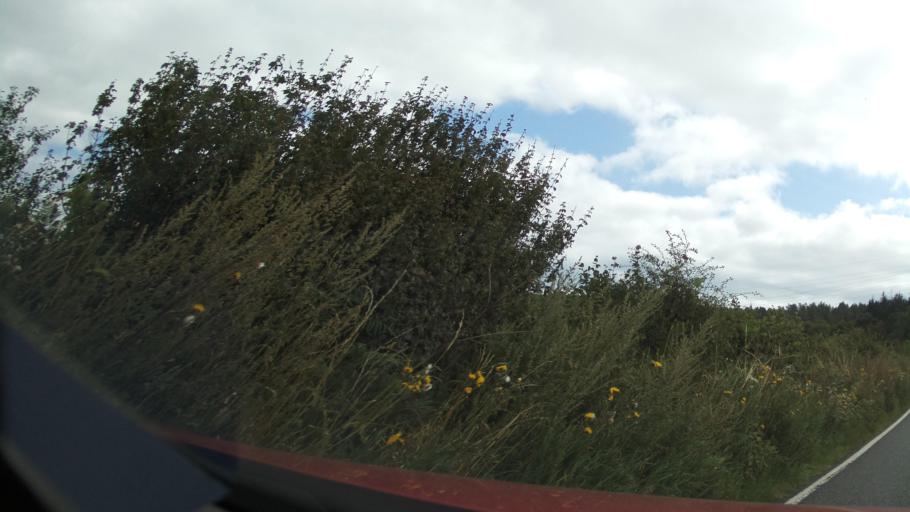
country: GB
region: England
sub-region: Devon
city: Bishopsteignton
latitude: 50.5891
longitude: -3.5330
